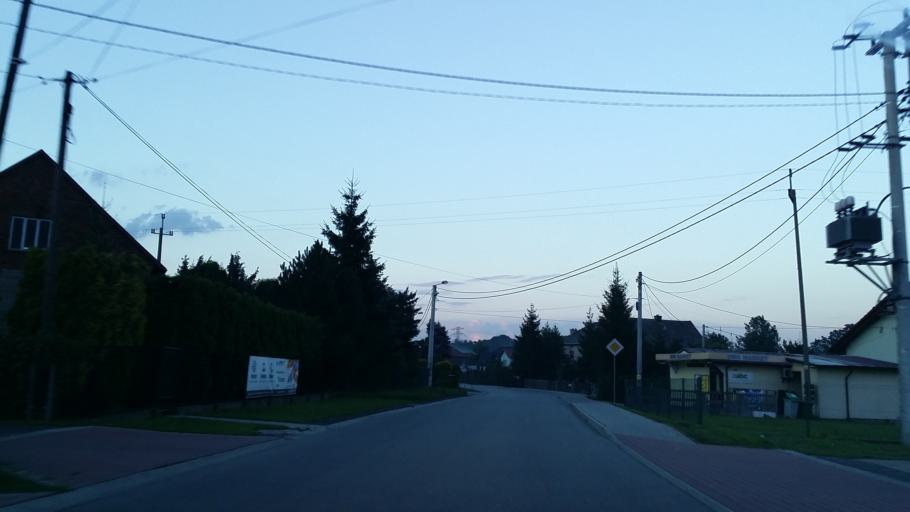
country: PL
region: Lesser Poland Voivodeship
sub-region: Powiat oswiecimski
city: Przeciszow
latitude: 50.0017
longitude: 19.3627
